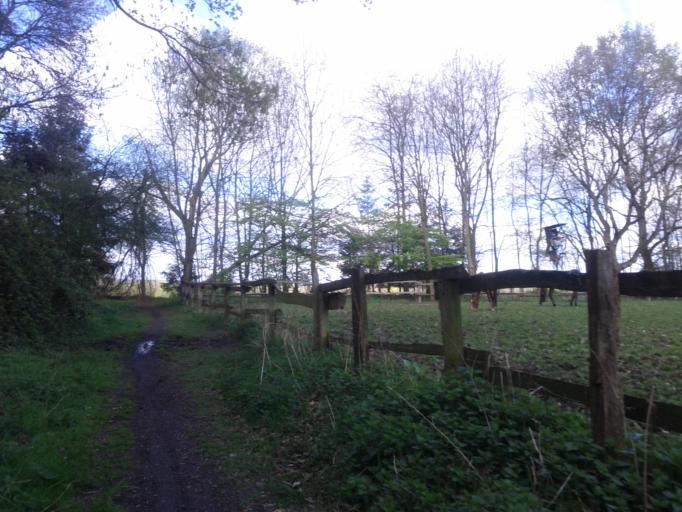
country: DE
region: North Rhine-Westphalia
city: Lanstrop
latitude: 51.5709
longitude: 7.5518
